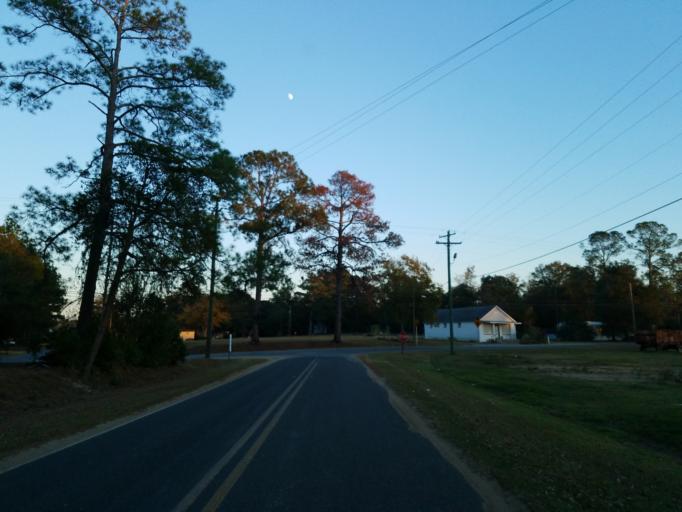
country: US
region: Georgia
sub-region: Irwin County
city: Ocilla
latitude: 31.6503
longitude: -83.3834
